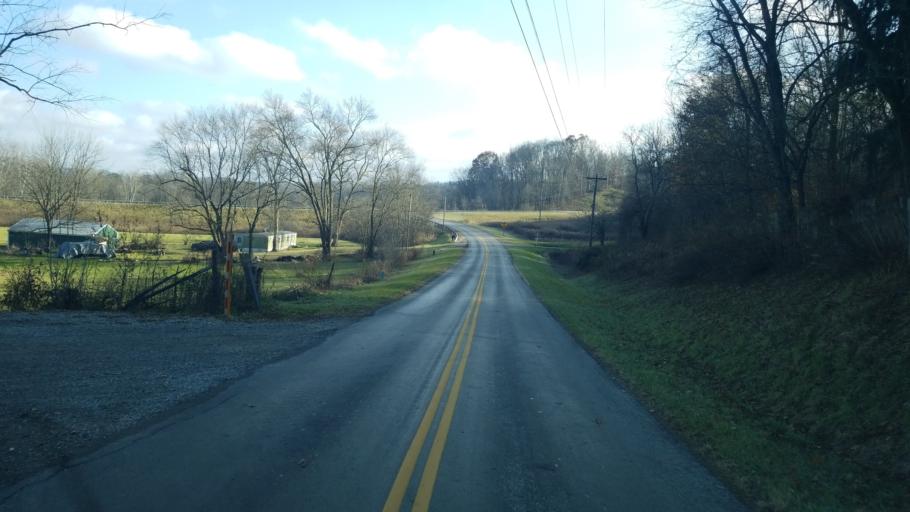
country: US
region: Ohio
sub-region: Ashland County
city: Loudonville
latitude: 40.6601
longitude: -82.3218
